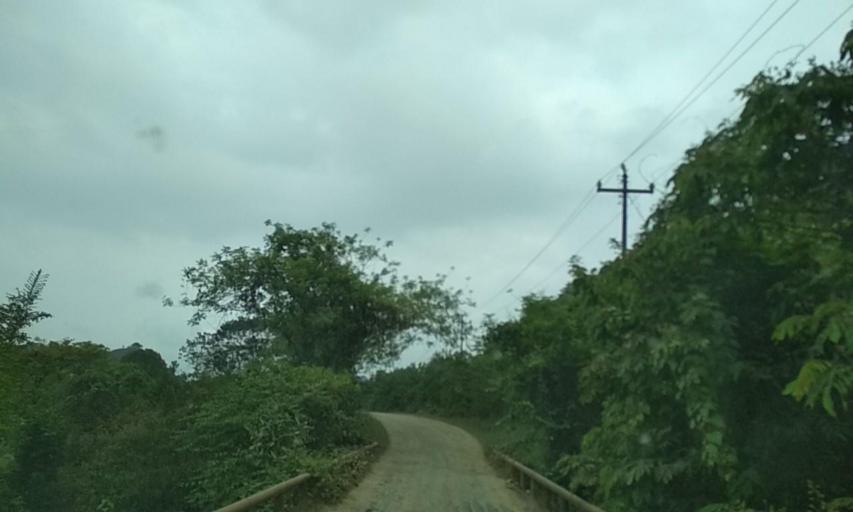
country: MX
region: Veracruz
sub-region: Uxpanapa
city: Poblado 10
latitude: 17.4547
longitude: -94.0912
